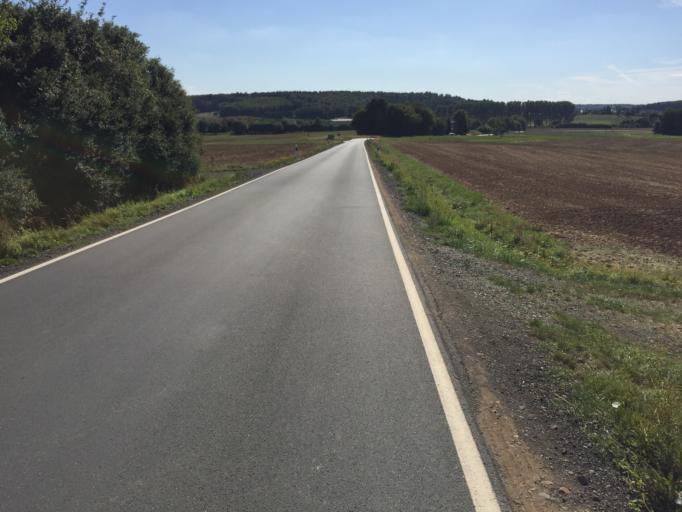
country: DE
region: Hesse
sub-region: Regierungsbezirk Giessen
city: Reiskirchen
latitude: 50.6039
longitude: 8.8501
